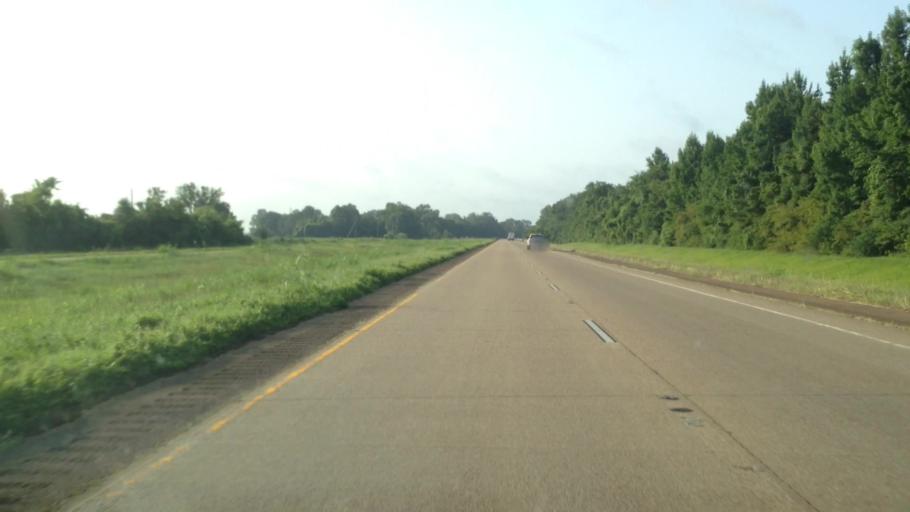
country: US
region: Louisiana
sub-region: Rapides Parish
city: Woodworth
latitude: 31.1376
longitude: -92.4496
